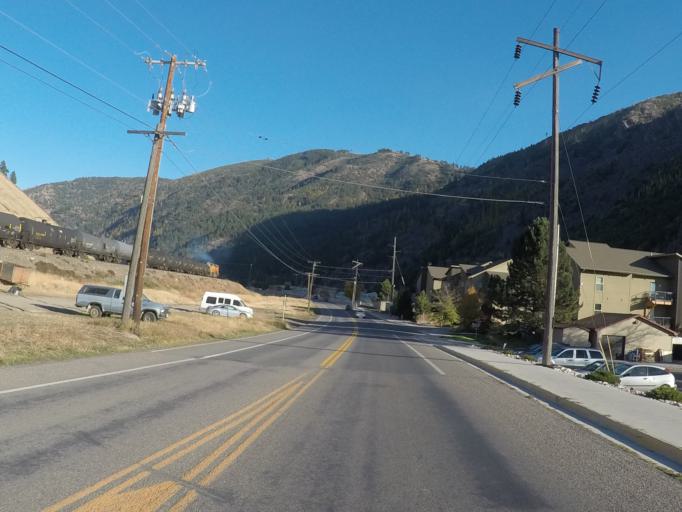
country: US
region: Montana
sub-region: Missoula County
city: Missoula
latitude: 46.8647
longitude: -113.9737
